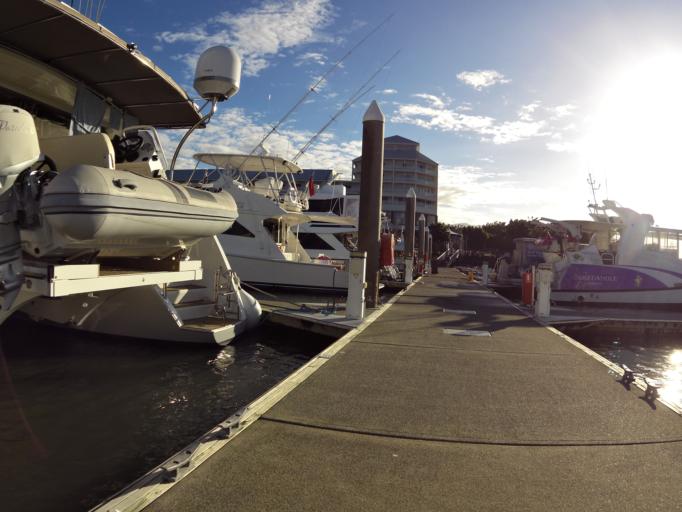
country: AU
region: Queensland
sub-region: Cairns
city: Cairns
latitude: -16.9191
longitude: 145.7817
